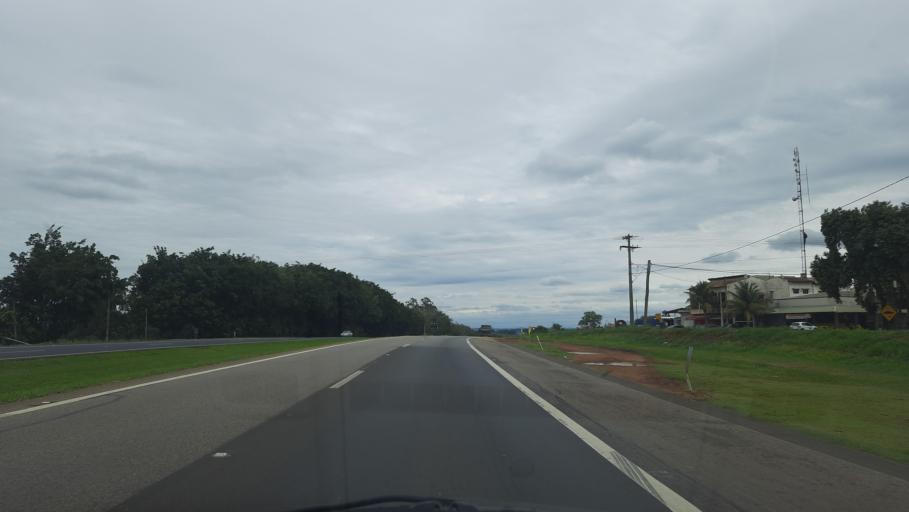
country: BR
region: Sao Paulo
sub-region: Moji-Guacu
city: Mogi-Gaucu
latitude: -22.2234
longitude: -46.9793
